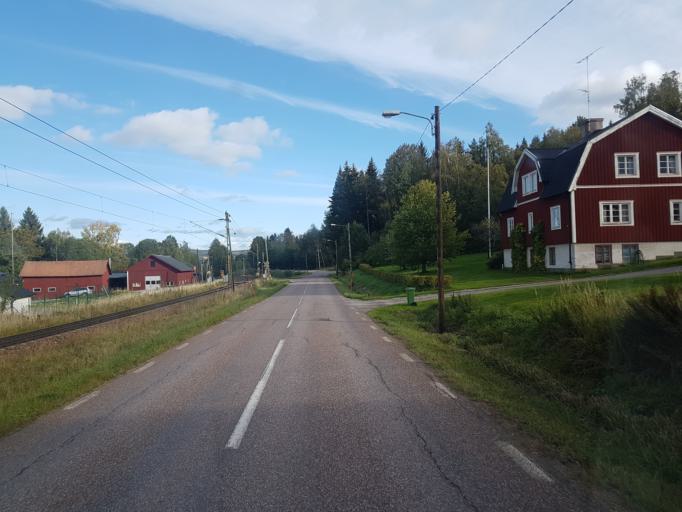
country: SE
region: Dalarna
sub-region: Saters Kommun
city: Saeter
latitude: 60.3651
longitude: 15.7208
